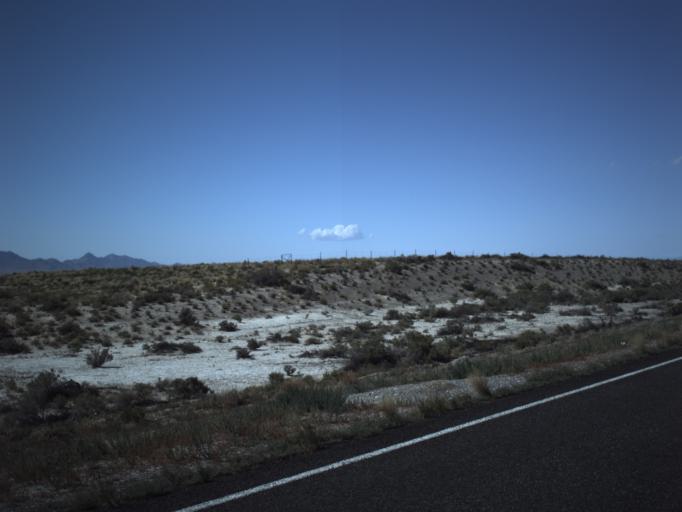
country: US
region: Utah
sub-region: Millard County
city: Delta
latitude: 39.1925
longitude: -112.9969
